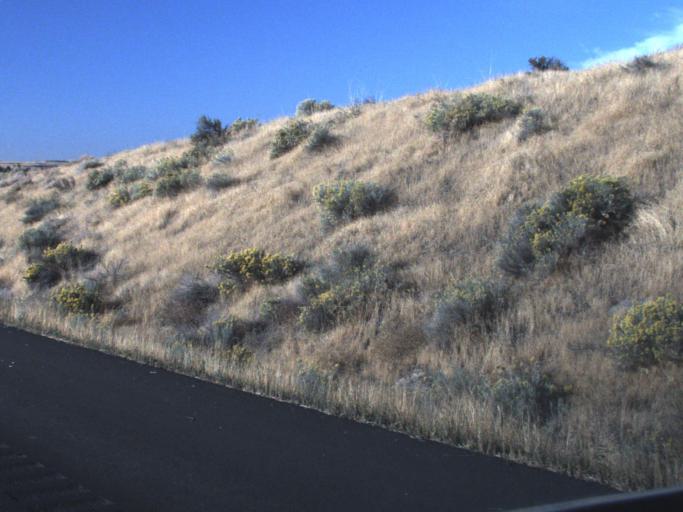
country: US
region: Washington
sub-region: Franklin County
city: Connell
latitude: 46.6666
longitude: -118.8485
